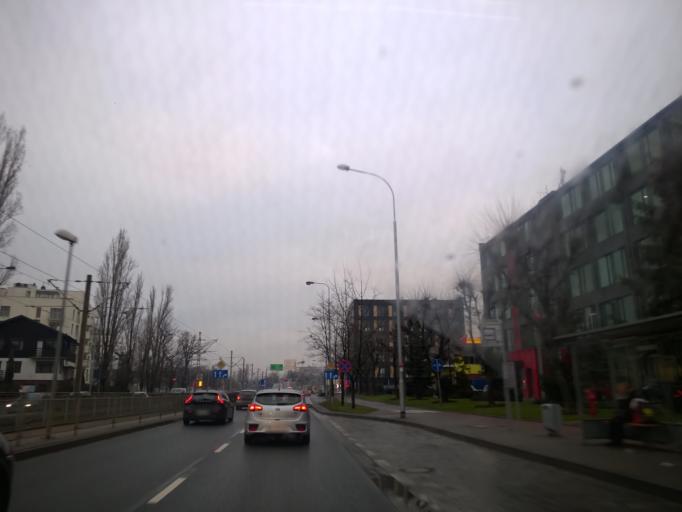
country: PL
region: Lower Silesian Voivodeship
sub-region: Powiat wroclawski
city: Wroclaw
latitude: 51.0818
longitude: 17.0232
